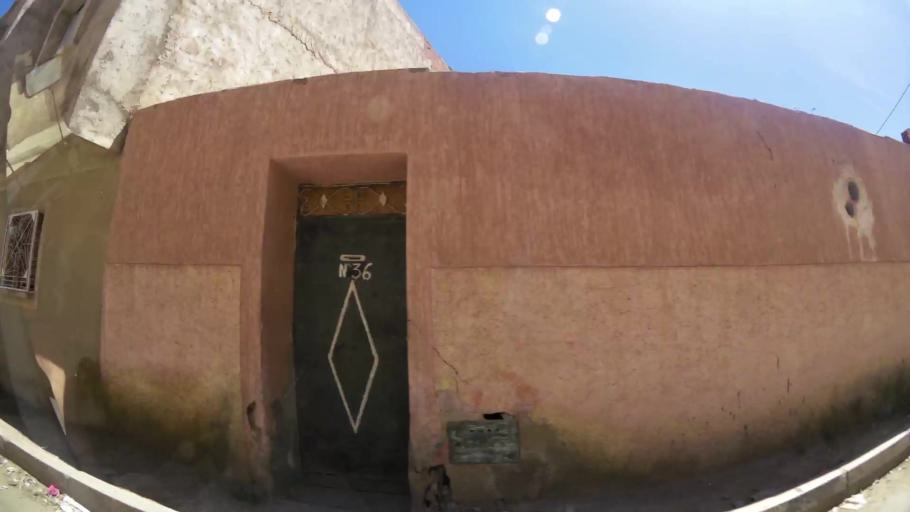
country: MA
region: Oriental
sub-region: Oujda-Angad
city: Oujda
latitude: 34.6603
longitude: -1.8833
